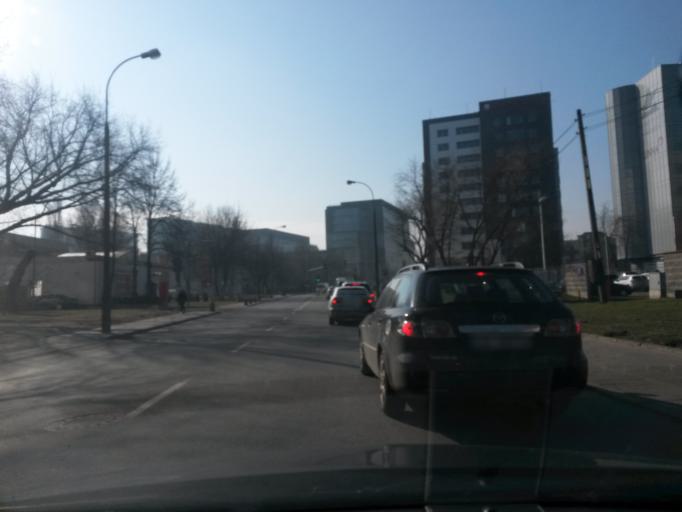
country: PL
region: Masovian Voivodeship
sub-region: Warszawa
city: Mokotow
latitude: 52.1812
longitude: 20.9977
